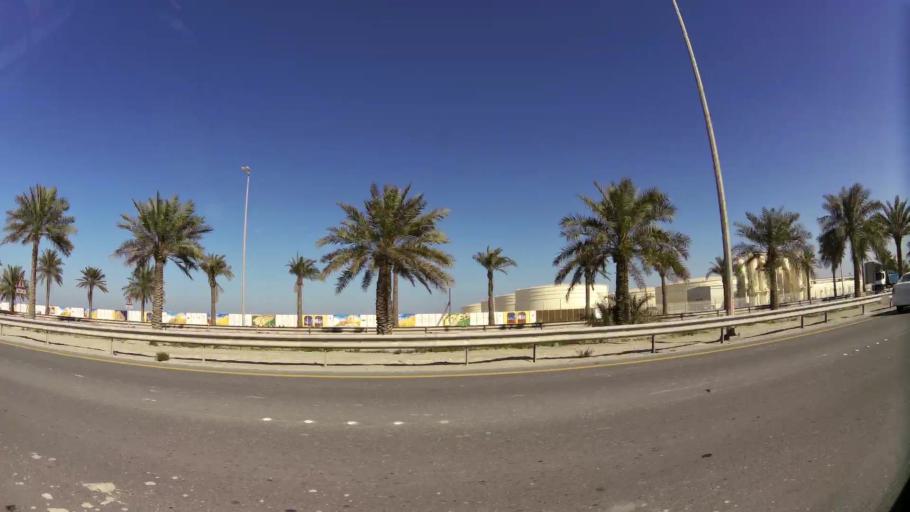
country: BH
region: Muharraq
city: Al Hadd
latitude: 26.2313
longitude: 50.6575
